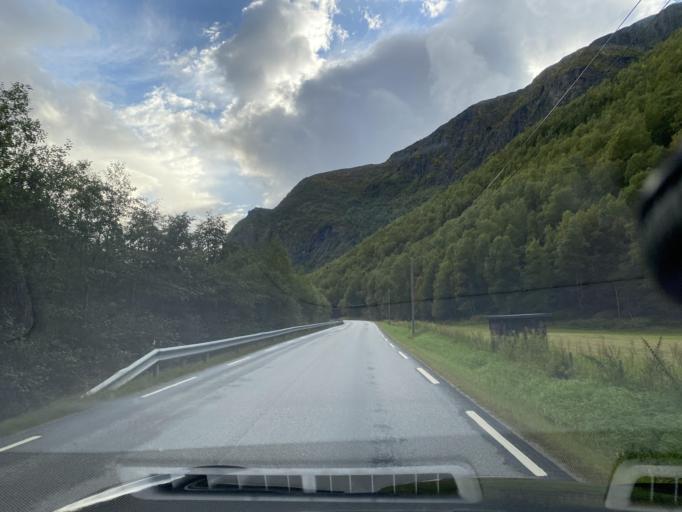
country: NO
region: Oppland
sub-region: Lom
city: Fossbergom
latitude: 61.7864
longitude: 8.4468
